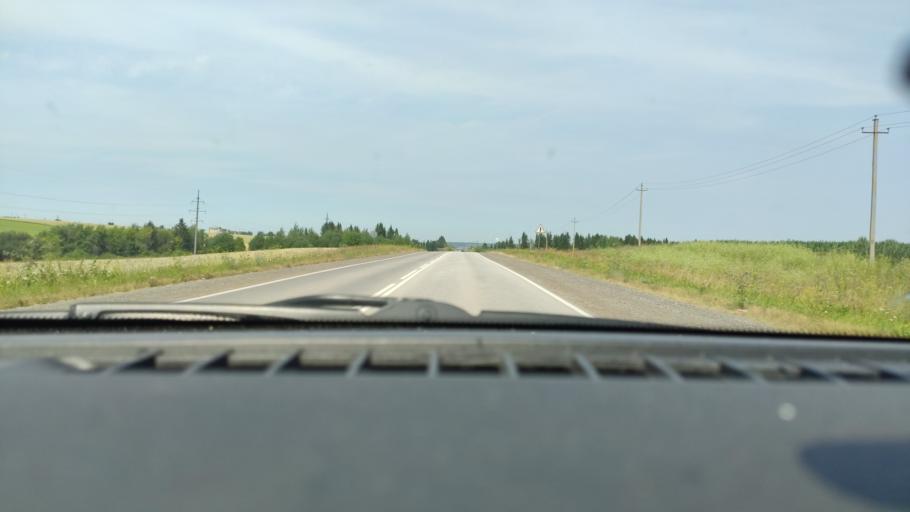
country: RU
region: Perm
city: Lobanovo
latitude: 57.8560
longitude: 56.2961
